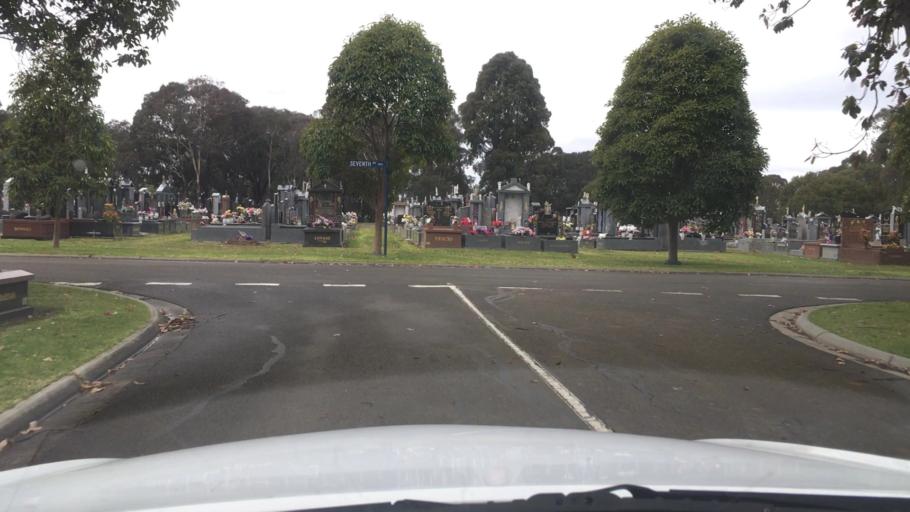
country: AU
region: Victoria
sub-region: Greater Dandenong
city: Noble Park North
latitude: -37.9427
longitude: 145.1844
